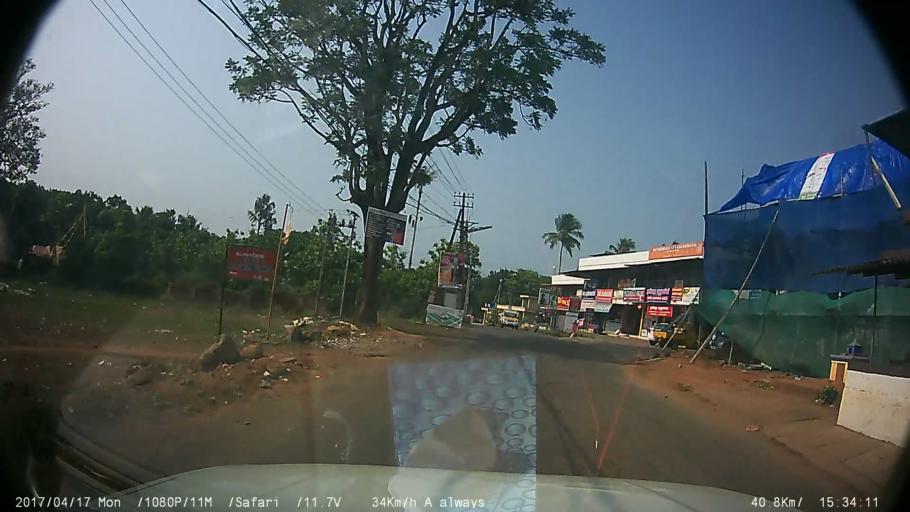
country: IN
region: Kerala
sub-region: Ernakulam
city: Ramamangalam
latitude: 9.9716
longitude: 76.4270
